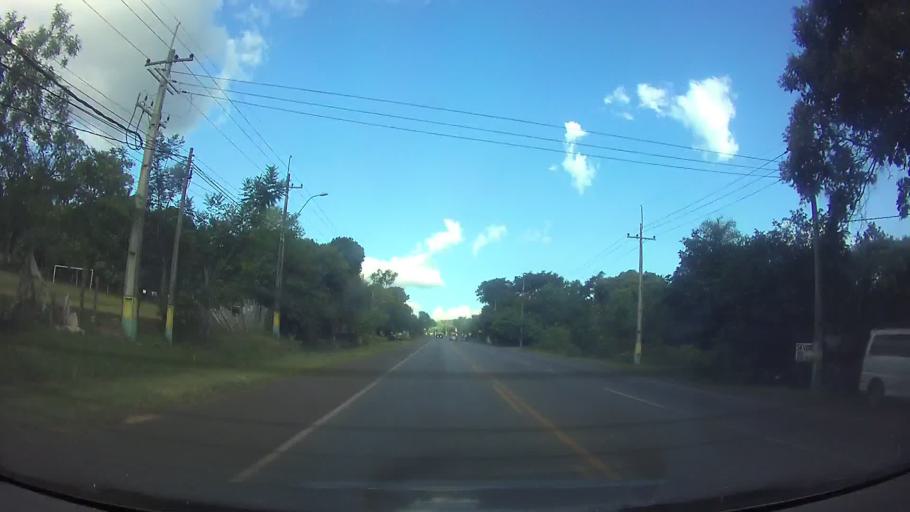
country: PY
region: Cordillera
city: Caacupe
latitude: -25.3874
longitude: -57.1162
